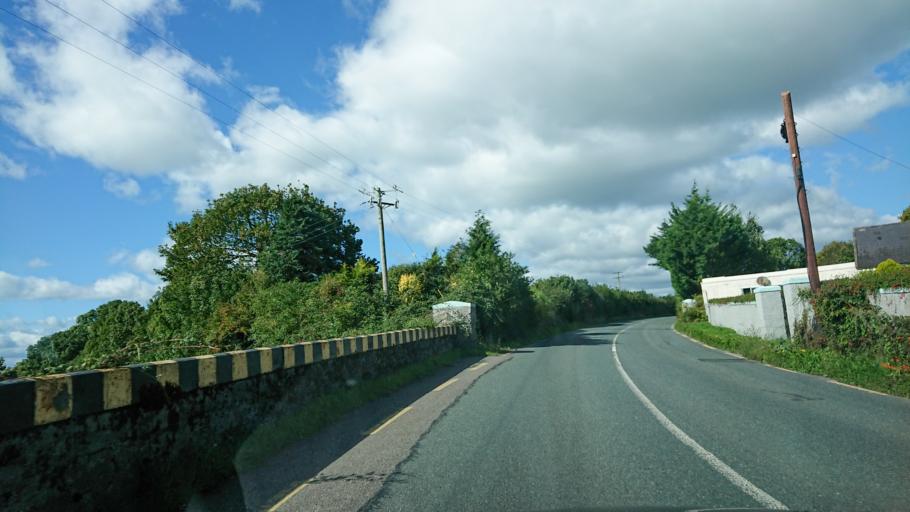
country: IE
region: Munster
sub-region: Waterford
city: Dungarvan
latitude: 52.1110
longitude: -7.6782
